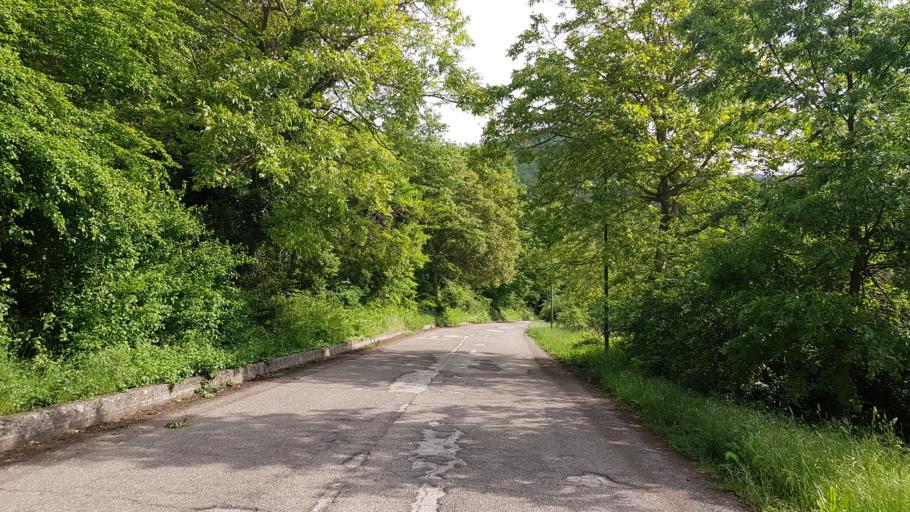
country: IT
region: Basilicate
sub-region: Provincia di Potenza
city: Rionero in Vulture
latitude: 40.9345
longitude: 15.6011
